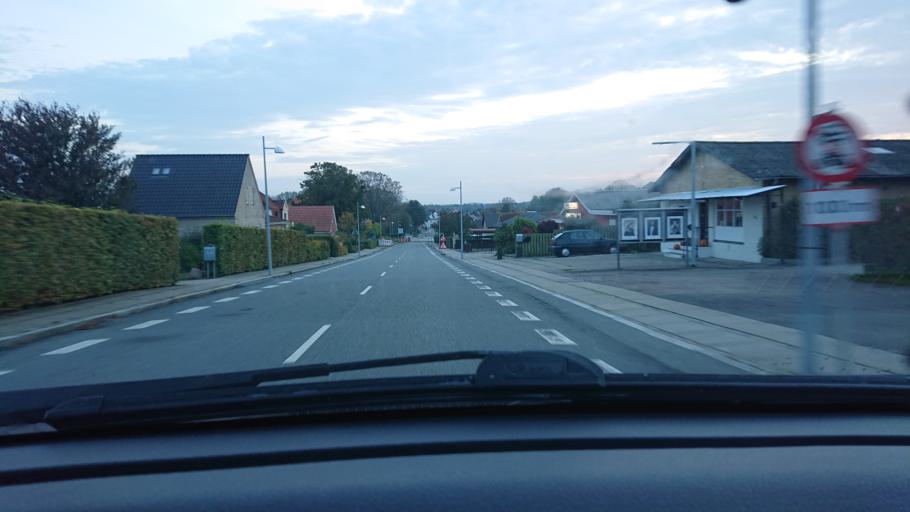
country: DK
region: South Denmark
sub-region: Nyborg Kommune
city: Ullerslev
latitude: 55.3582
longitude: 10.6711
